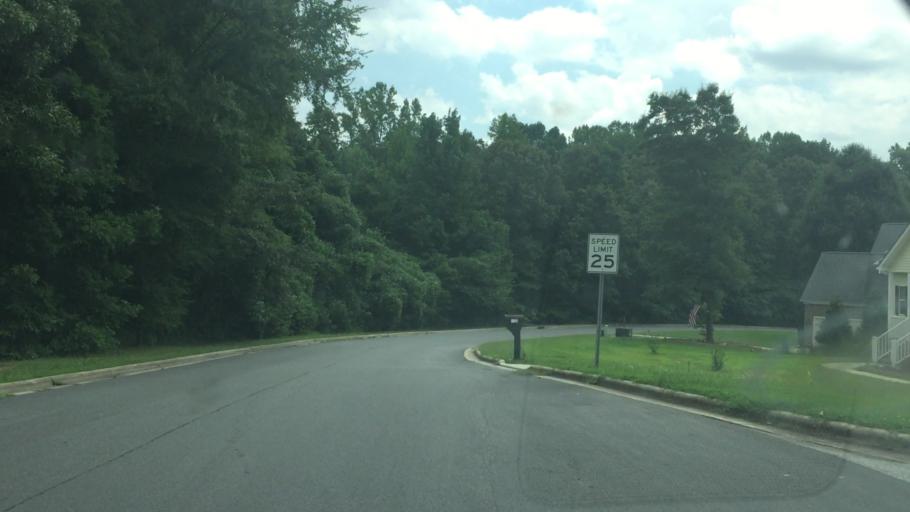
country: US
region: North Carolina
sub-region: Iredell County
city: Mooresville
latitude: 35.5879
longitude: -80.7936
